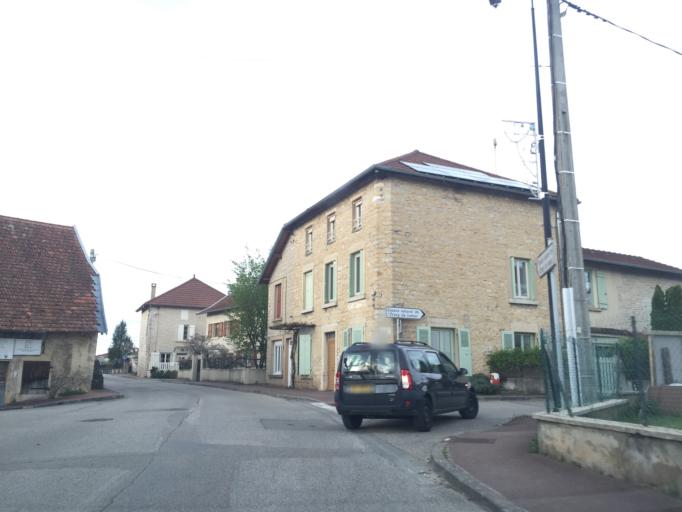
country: FR
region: Rhone-Alpes
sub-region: Departement de l'Isere
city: Hieres-sur-Amby
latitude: 45.7524
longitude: 5.3298
